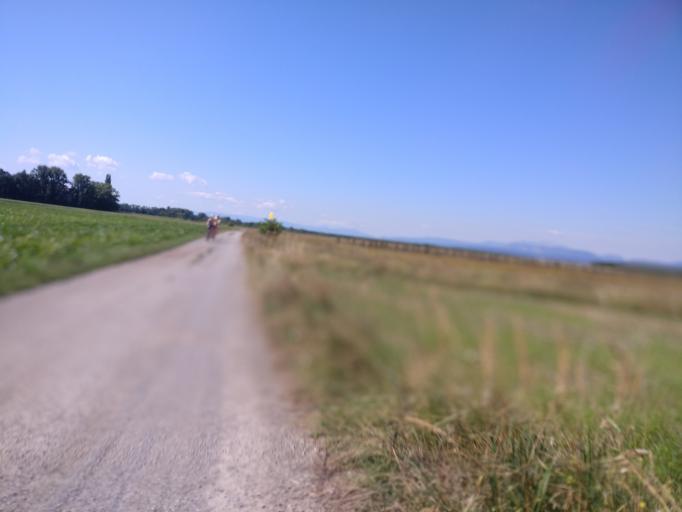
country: AT
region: Lower Austria
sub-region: Politischer Bezirk Baden
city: Pottendorf
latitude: 47.9165
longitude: 16.3579
